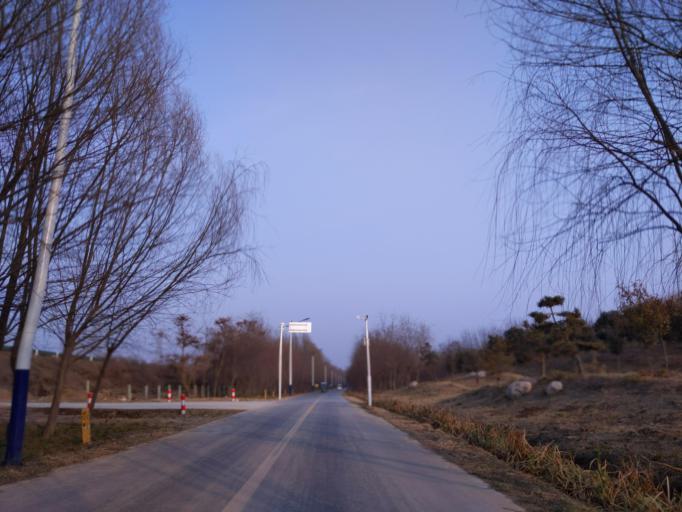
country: CN
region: Henan Sheng
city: Puyang
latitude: 35.8212
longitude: 115.0120
